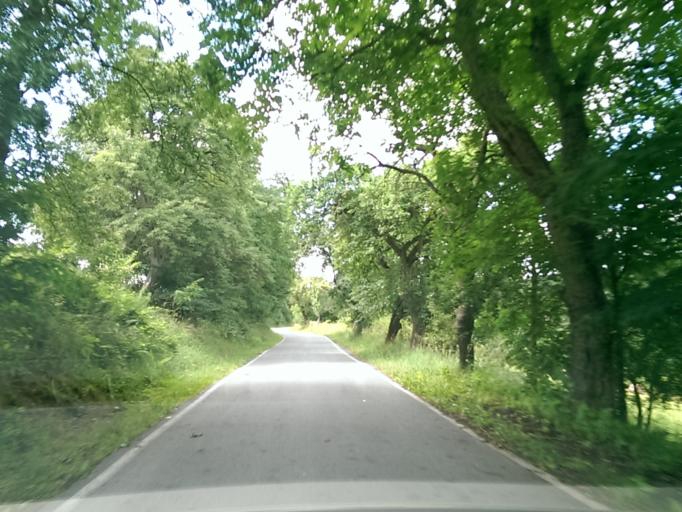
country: CZ
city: Duba
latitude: 50.4994
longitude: 14.5119
